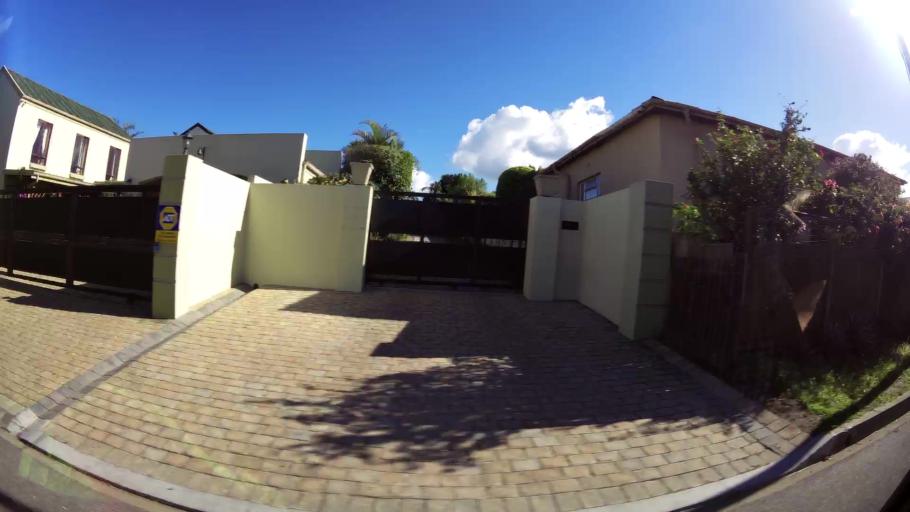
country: ZA
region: Western Cape
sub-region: Eden District Municipality
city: George
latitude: -33.9446
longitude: 22.4092
